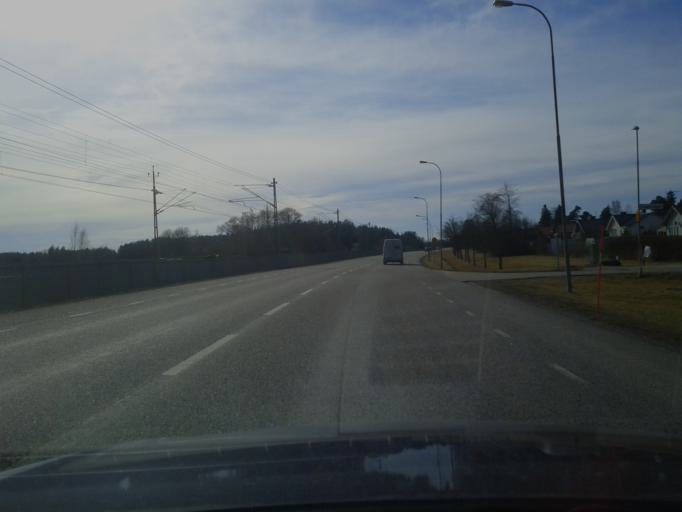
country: SE
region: Soedermanland
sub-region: Eskilstuna Kommun
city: Kvicksund
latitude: 59.5712
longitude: 16.3880
